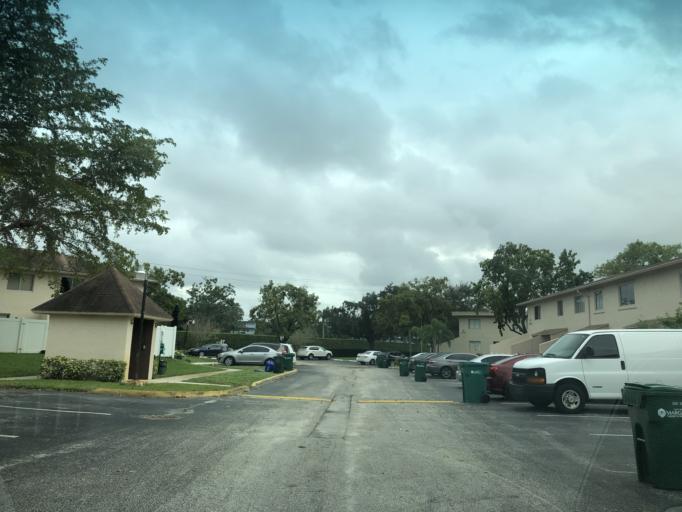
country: US
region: Florida
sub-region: Broward County
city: Margate
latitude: 26.2491
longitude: -80.2326
